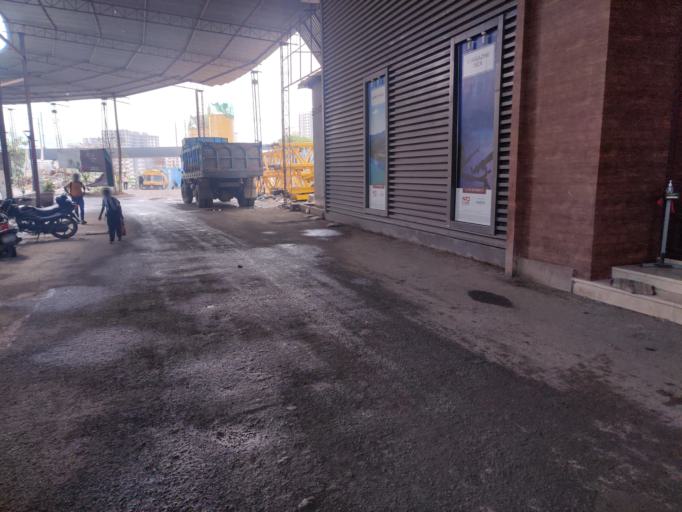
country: IN
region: Maharashtra
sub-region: Mumbai Suburban
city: Borivli
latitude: 19.2486
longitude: 72.8639
